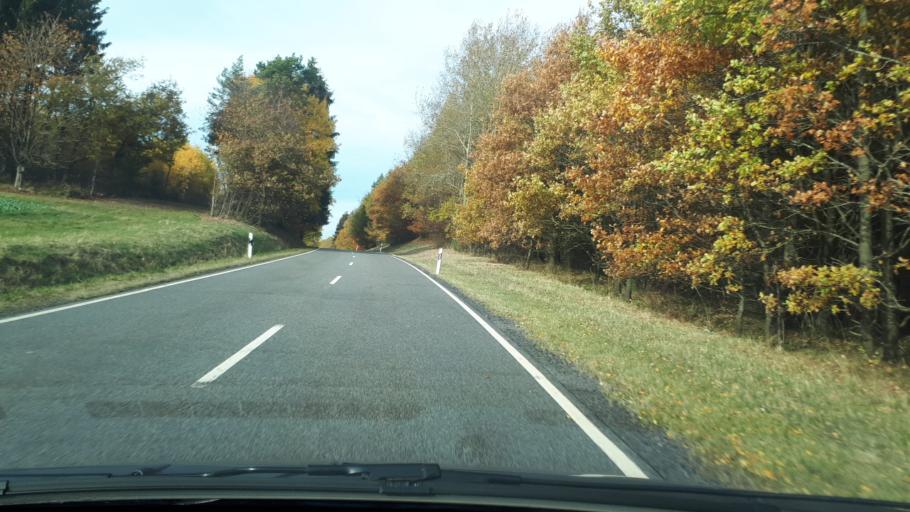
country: DE
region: Rheinland-Pfalz
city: Laubach
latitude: 50.2314
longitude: 7.0853
